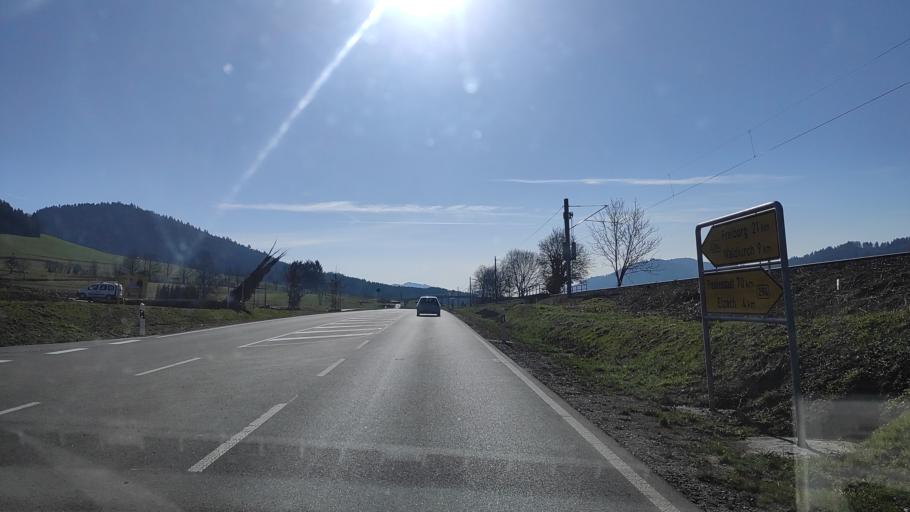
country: DE
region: Baden-Wuerttemberg
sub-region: Freiburg Region
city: Elzach
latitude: 48.1441
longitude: 8.0286
